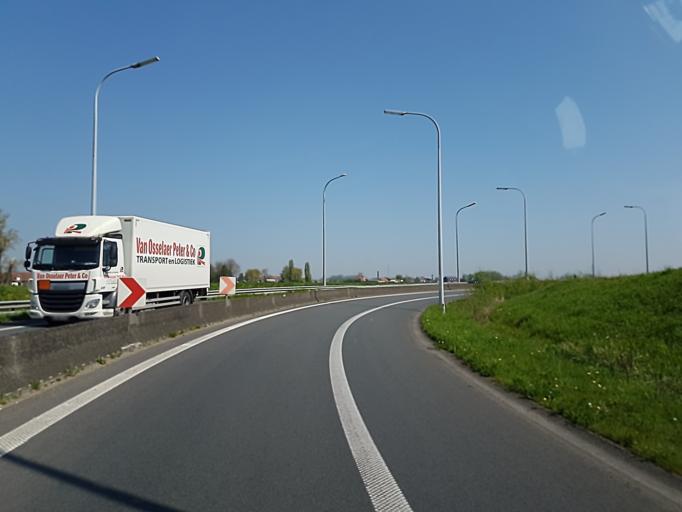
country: BE
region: Flanders
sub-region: Provincie West-Vlaanderen
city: Menen
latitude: 50.8181
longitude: 3.0975
